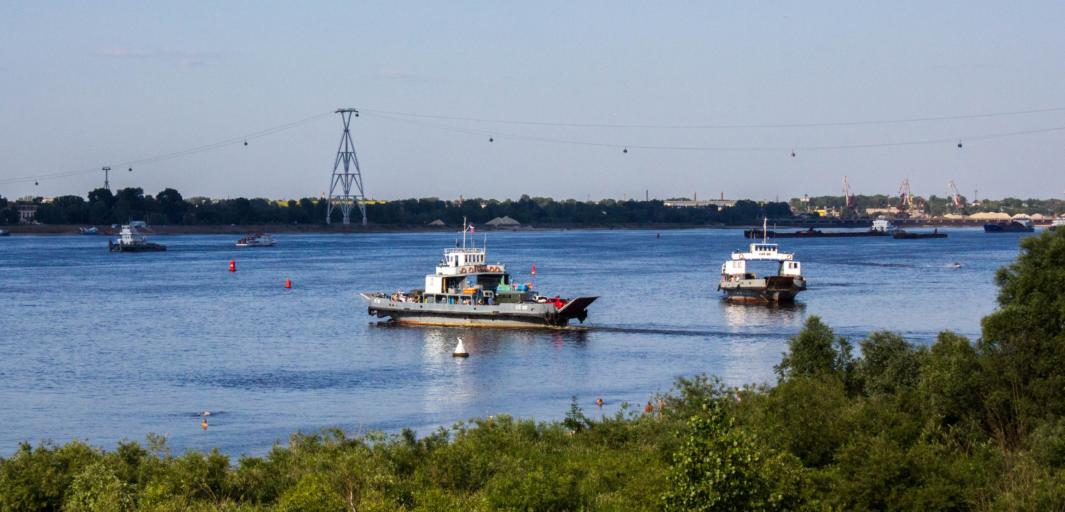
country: RU
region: Nizjnij Novgorod
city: Nizhniy Novgorod
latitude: 56.3314
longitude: 44.0185
